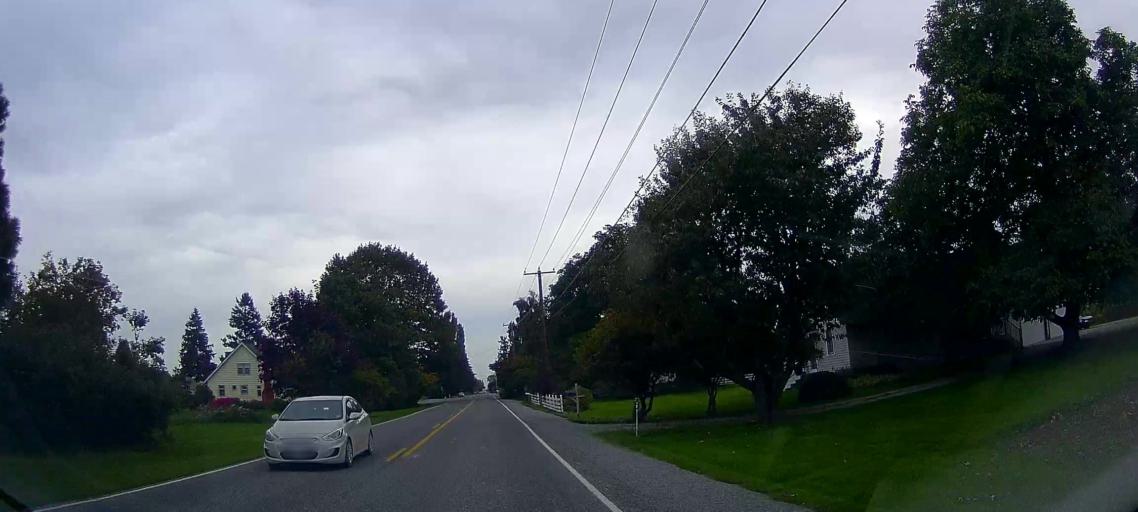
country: US
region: Washington
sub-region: Skagit County
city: Mount Vernon
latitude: 48.4475
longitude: -122.3786
